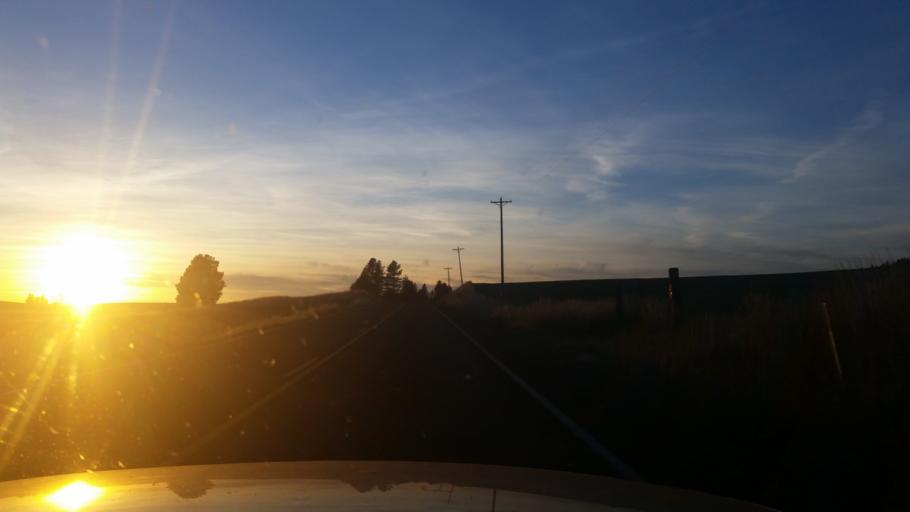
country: US
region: Washington
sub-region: Spokane County
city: Veradale
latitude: 47.5075
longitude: -117.1403
